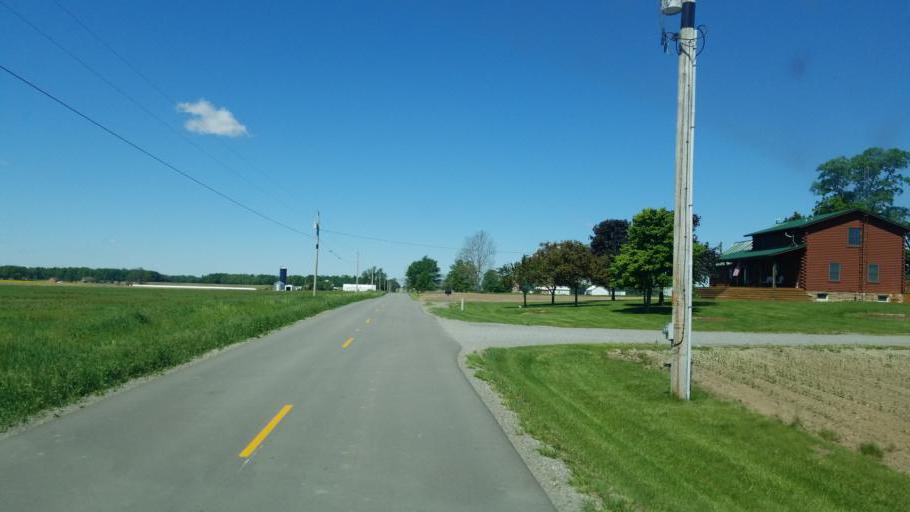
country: US
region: Ohio
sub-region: Shelby County
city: Jackson Center
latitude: 40.4174
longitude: -83.9807
